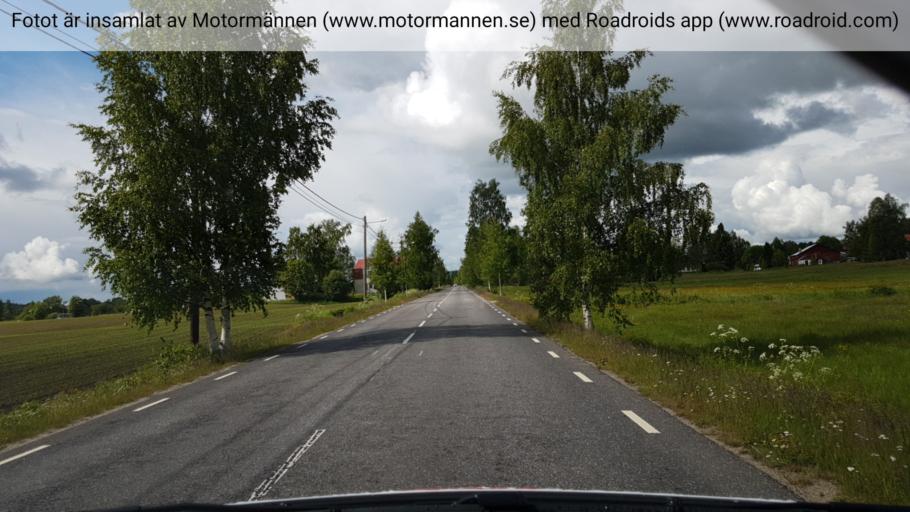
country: SE
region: Vaesterbotten
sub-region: Vannas Kommun
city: Vannasby
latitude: 63.8995
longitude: 19.8733
